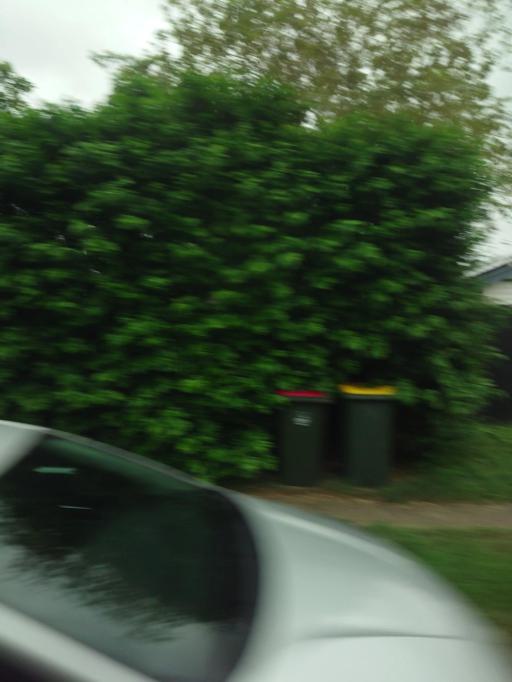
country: AU
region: Queensland
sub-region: Brisbane
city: Seven Hills
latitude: -27.4765
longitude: 153.0685
